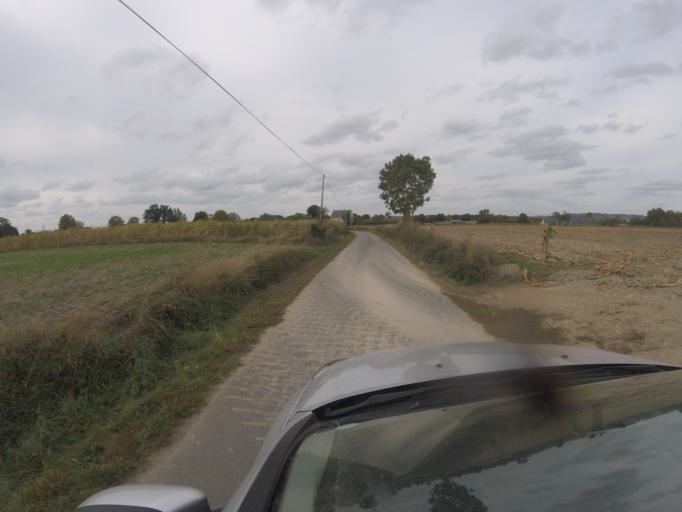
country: FR
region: Lower Normandy
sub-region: Departement de la Manche
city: Le Val-Saint-Pere
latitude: 48.6355
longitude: -1.3889
